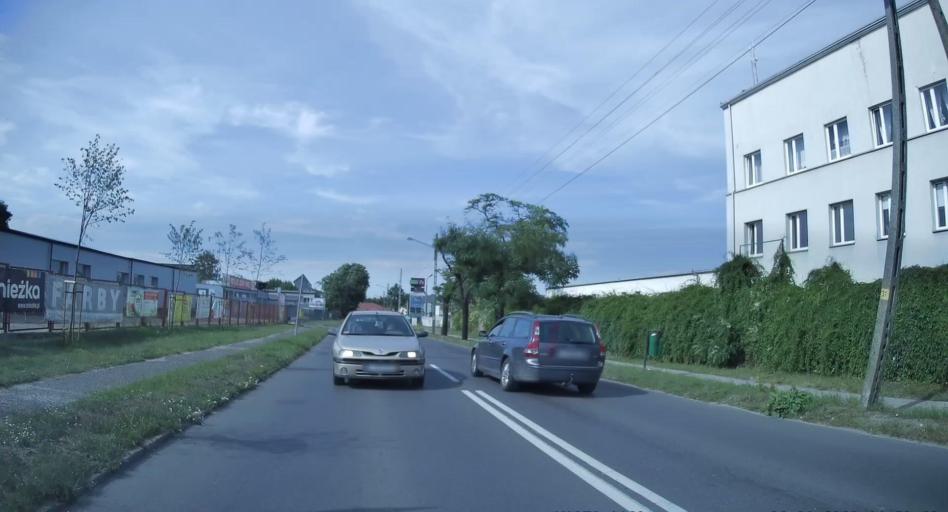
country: PL
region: Lodz Voivodeship
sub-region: Powiat tomaszowski
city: Tomaszow Mazowiecki
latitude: 51.5325
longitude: 19.9968
